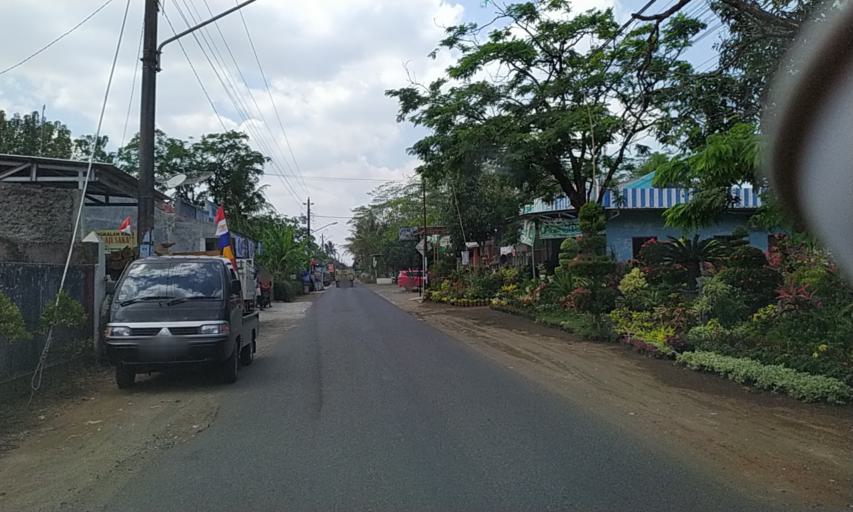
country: ID
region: Central Java
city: Kroya
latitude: -7.6394
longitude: 109.2431
